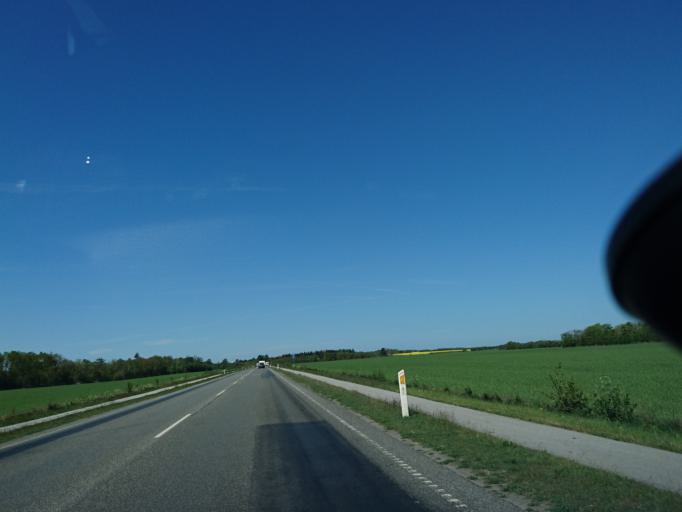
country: DK
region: North Denmark
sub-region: Hjorring Kommune
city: Tars
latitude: 57.4560
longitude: 10.0932
